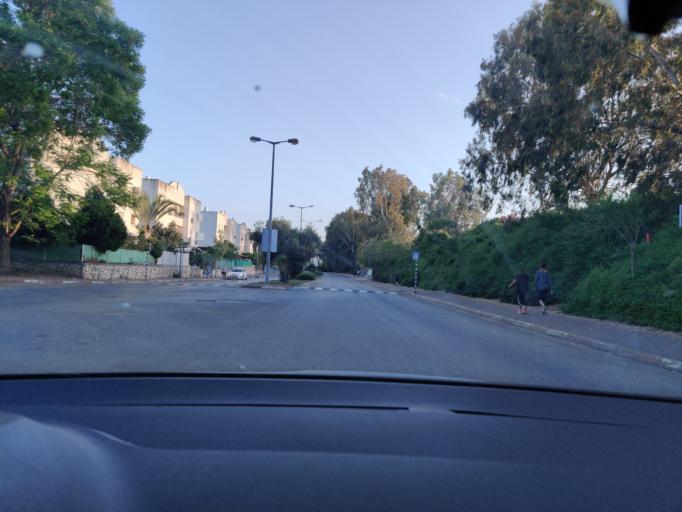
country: IL
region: Haifa
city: Hadera
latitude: 32.4762
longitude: 34.9525
